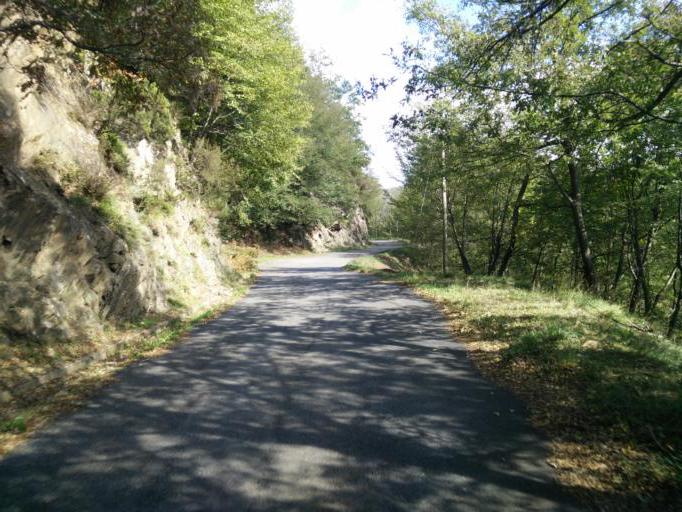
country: IT
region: Tuscany
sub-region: Provincia di Massa-Carrara
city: Patigno
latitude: 44.3470
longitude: 9.7097
